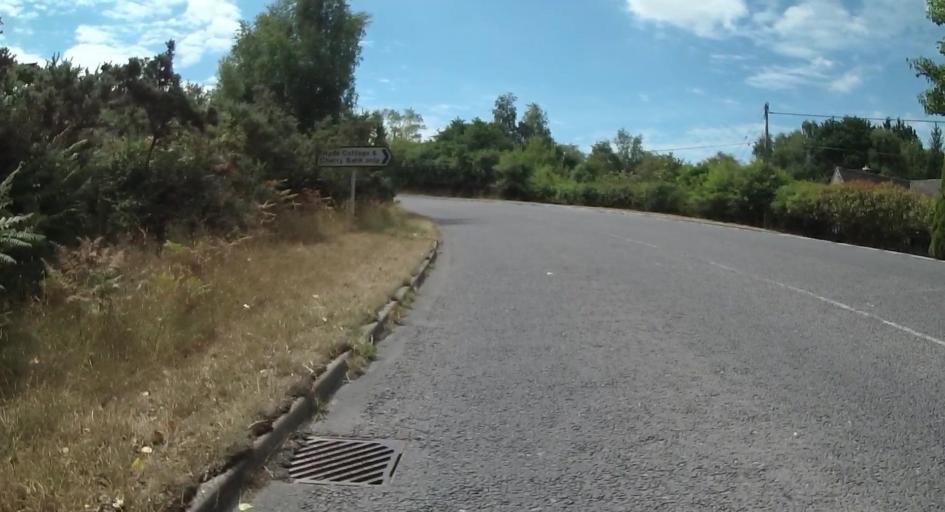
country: GB
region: England
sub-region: Dorset
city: Wareham
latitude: 50.6673
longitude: -2.1037
